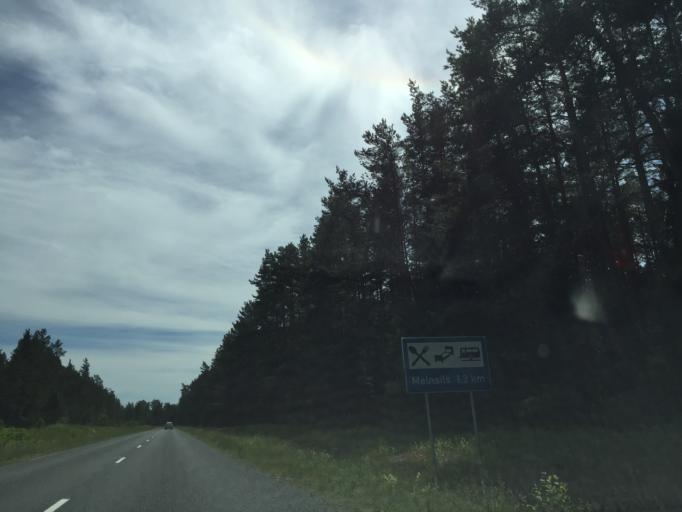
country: LV
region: Dundaga
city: Dundaga
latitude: 57.6641
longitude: 22.5705
